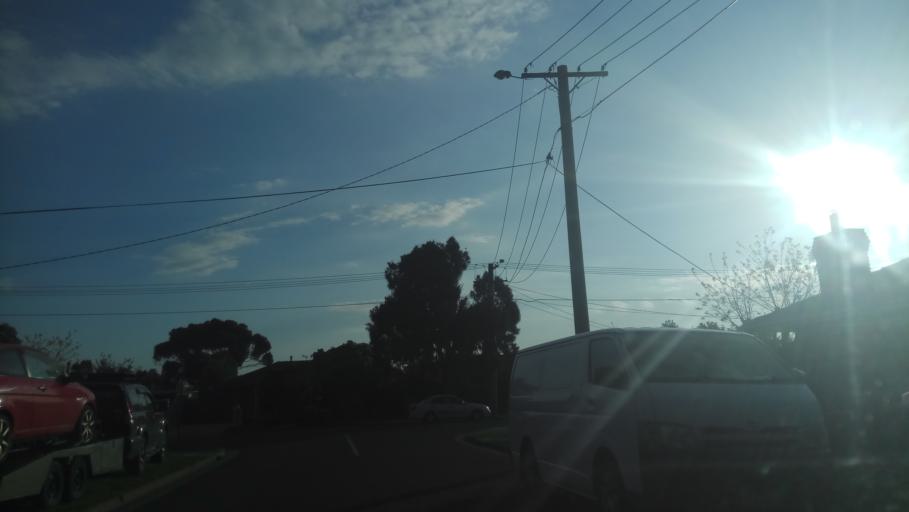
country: AU
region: Victoria
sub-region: Hobsons Bay
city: Altona Meadows
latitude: -37.8919
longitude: 144.7817
